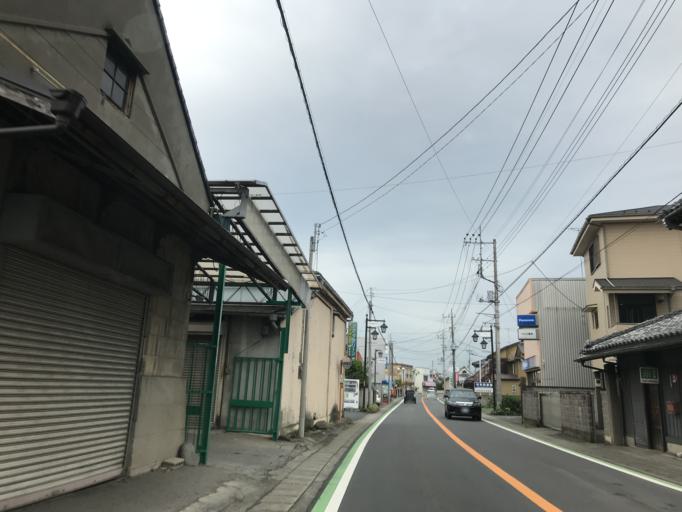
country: JP
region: Ibaraki
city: Sakai
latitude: 36.1040
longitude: 139.7976
